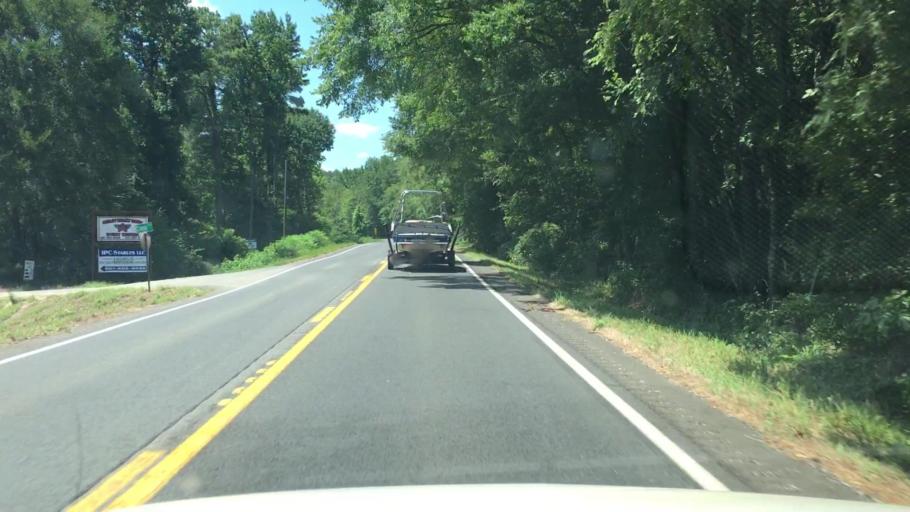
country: US
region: Arkansas
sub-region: Garland County
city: Lake Hamilton
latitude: 34.3371
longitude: -93.1799
